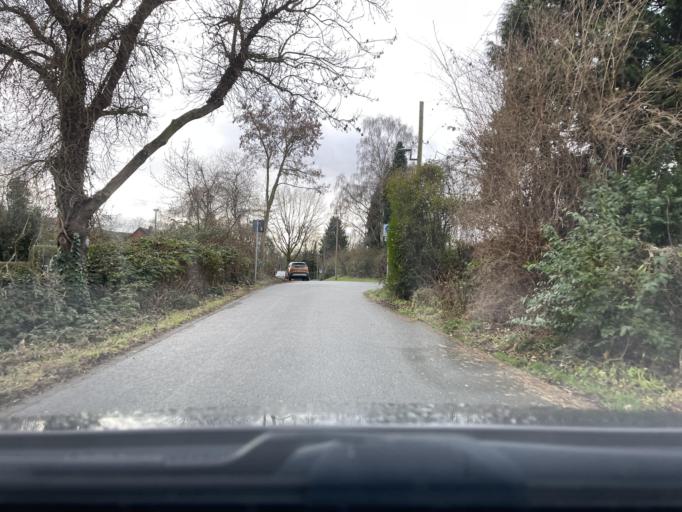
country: DE
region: North Rhine-Westphalia
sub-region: Regierungsbezirk Dusseldorf
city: Essen
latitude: 51.4608
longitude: 6.9547
